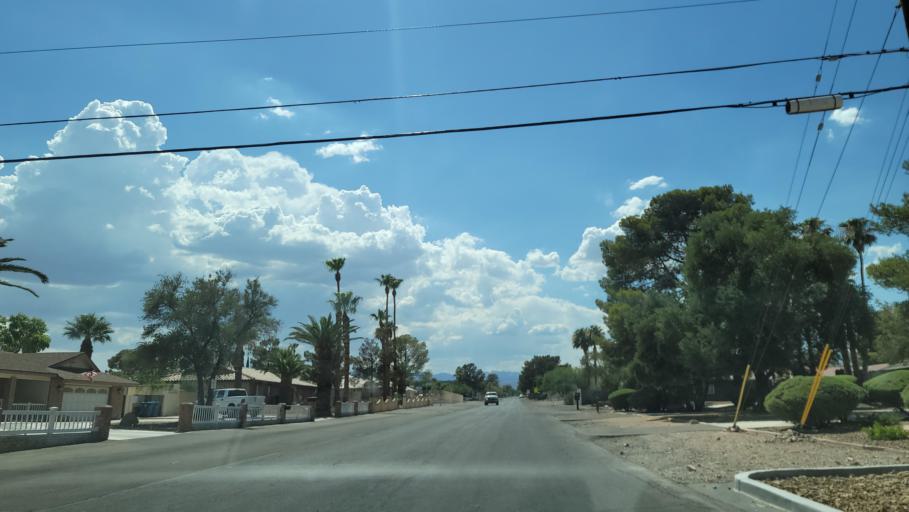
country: US
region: Nevada
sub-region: Clark County
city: Spring Valley
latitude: 36.1386
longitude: -115.2305
